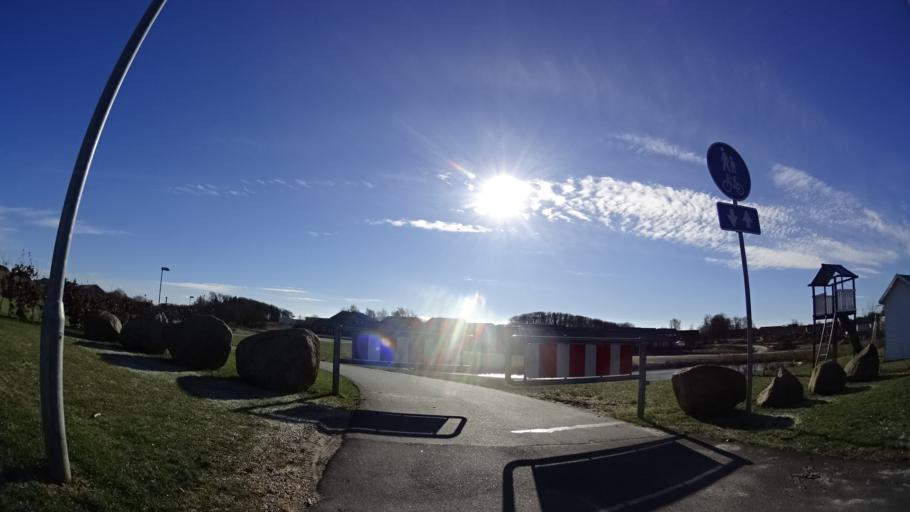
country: DK
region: Central Jutland
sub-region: Arhus Kommune
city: Kolt
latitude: 56.1157
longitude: 10.0882
